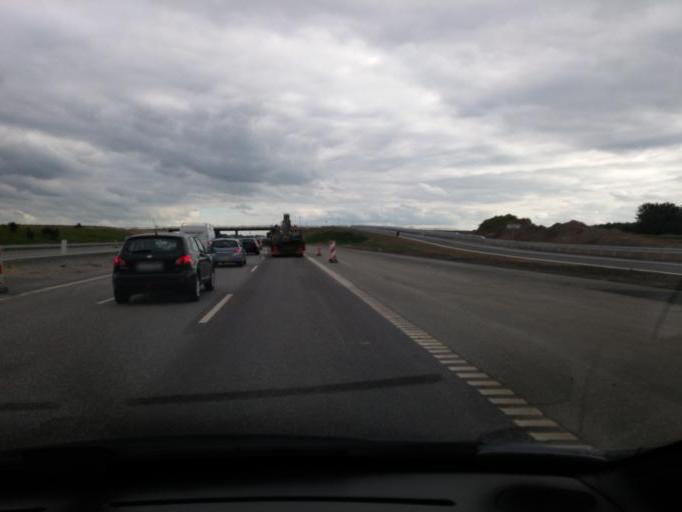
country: DK
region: Zealand
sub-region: Solrod Kommune
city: Solrod
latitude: 55.5076
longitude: 12.1774
